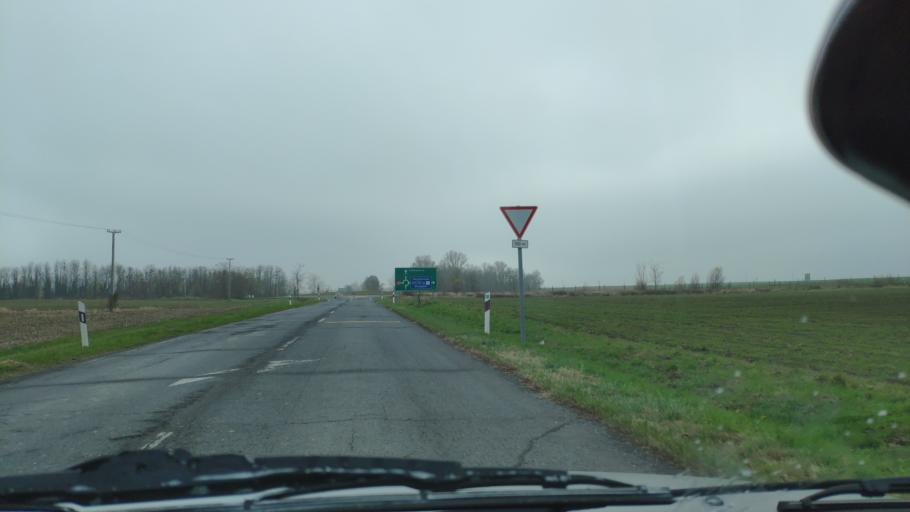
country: HU
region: Zala
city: Zalakomar
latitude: 46.5893
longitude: 17.2634
